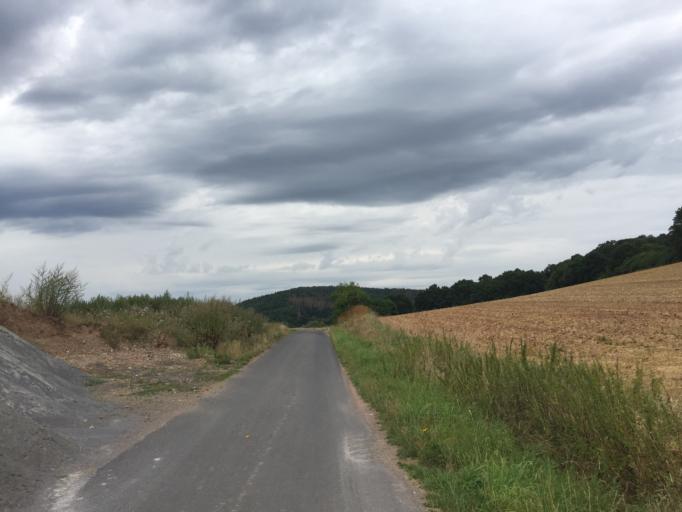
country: DE
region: Hesse
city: Breitenbach
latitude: 50.9268
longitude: 9.7899
